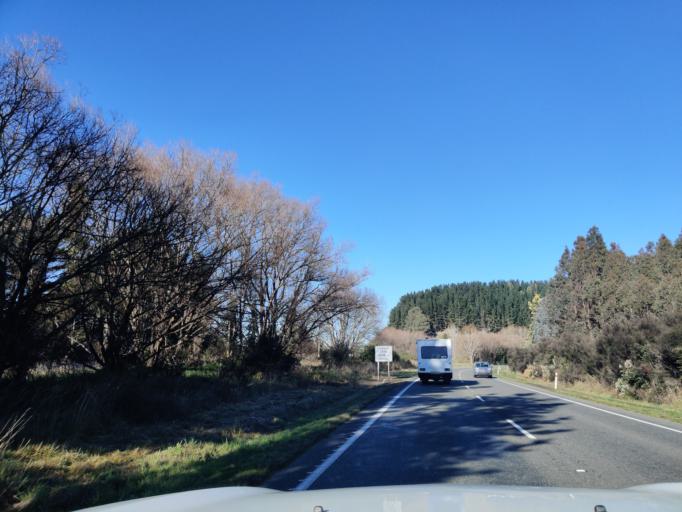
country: NZ
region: Manawatu-Wanganui
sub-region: Ruapehu District
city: Waiouru
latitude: -39.7563
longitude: 175.8294
